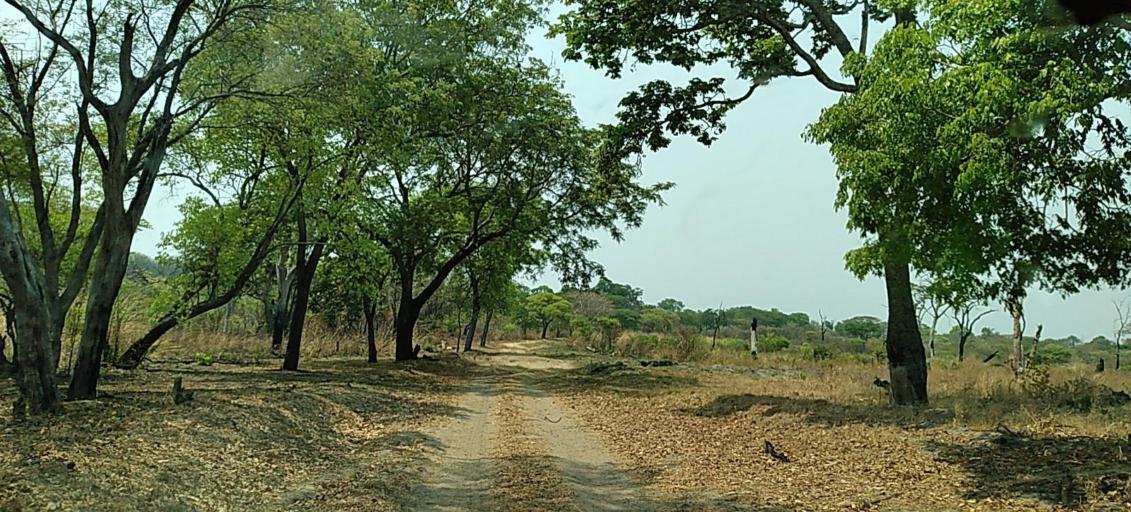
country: ZM
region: Western
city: Lukulu
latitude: -13.9677
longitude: 23.2285
